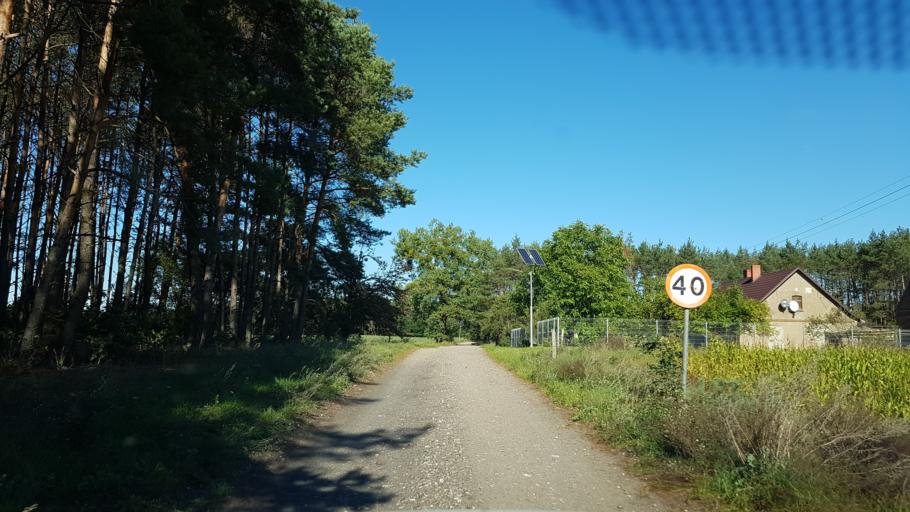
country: PL
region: Lubusz
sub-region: Powiat gorzowski
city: Lubiszyn
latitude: 52.8374
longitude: 14.9289
